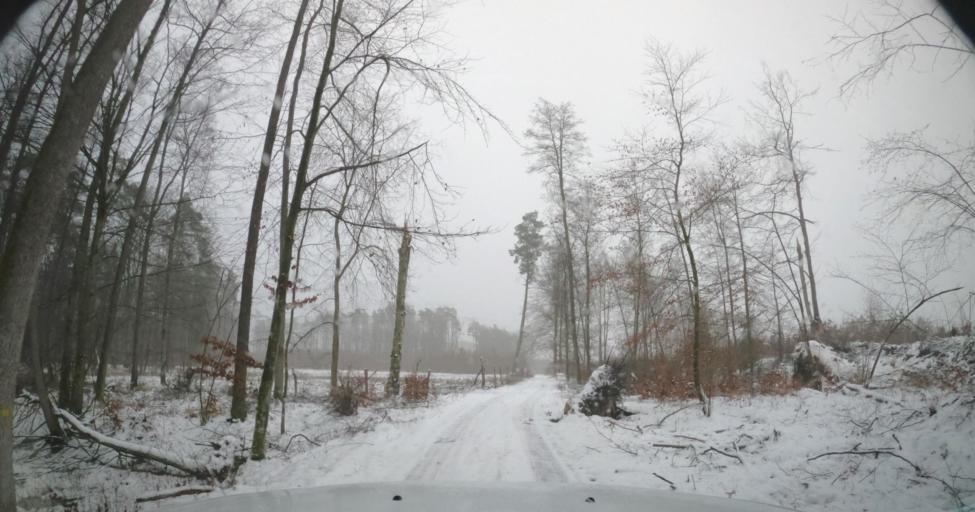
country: PL
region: West Pomeranian Voivodeship
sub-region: Powiat goleniowski
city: Przybiernow
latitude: 53.7104
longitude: 14.8793
